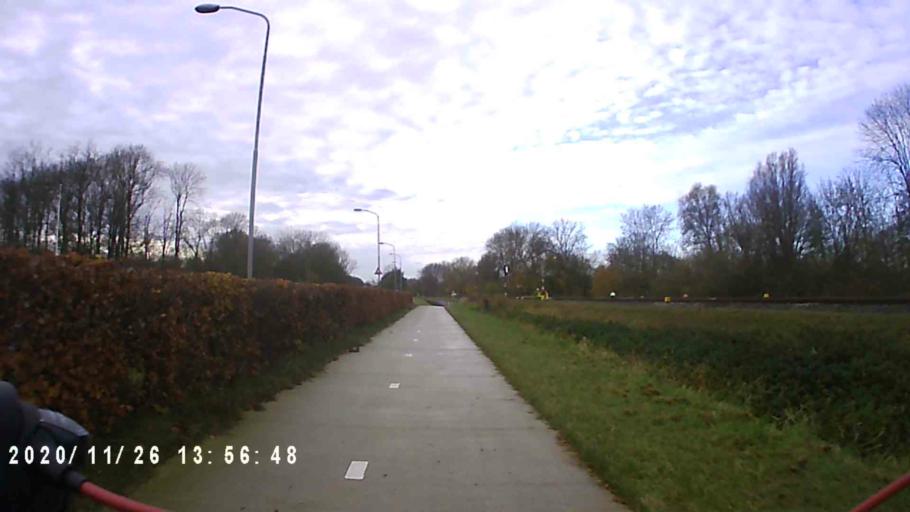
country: NL
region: Groningen
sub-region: Gemeente Delfzijl
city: Delfzijl
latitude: 53.3330
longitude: 6.9151
